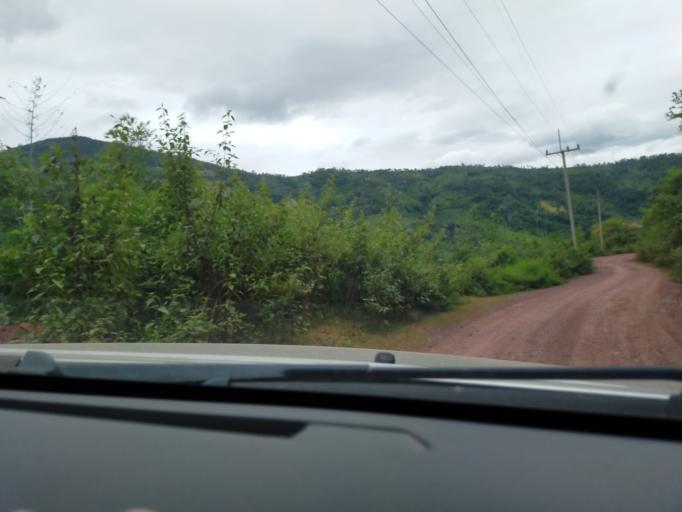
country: TH
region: Nan
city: Chaloem Phra Kiat
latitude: 19.7821
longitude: 101.3605
